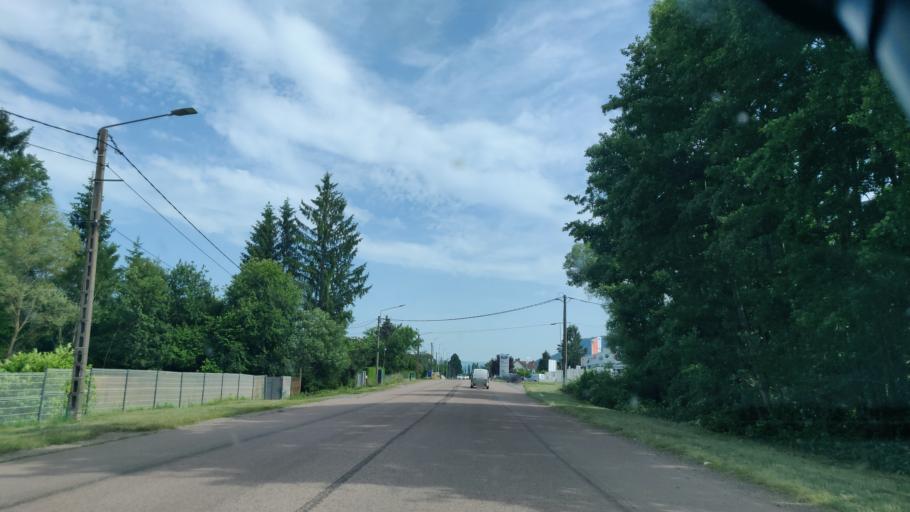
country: FR
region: Lorraine
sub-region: Departement des Vosges
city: Saint-Michel-sur-Meurthe
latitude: 48.3086
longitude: 6.9232
